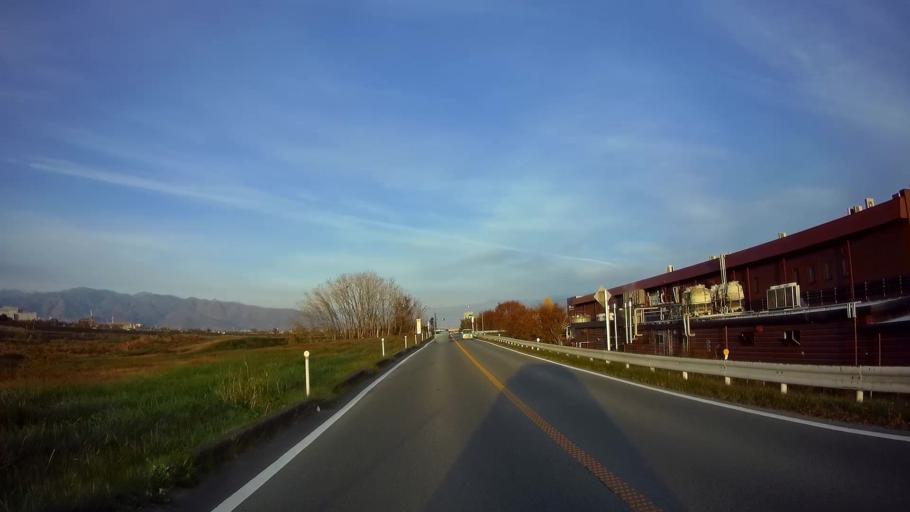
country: JP
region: Yamanashi
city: Kofu-shi
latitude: 35.5923
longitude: 138.5622
